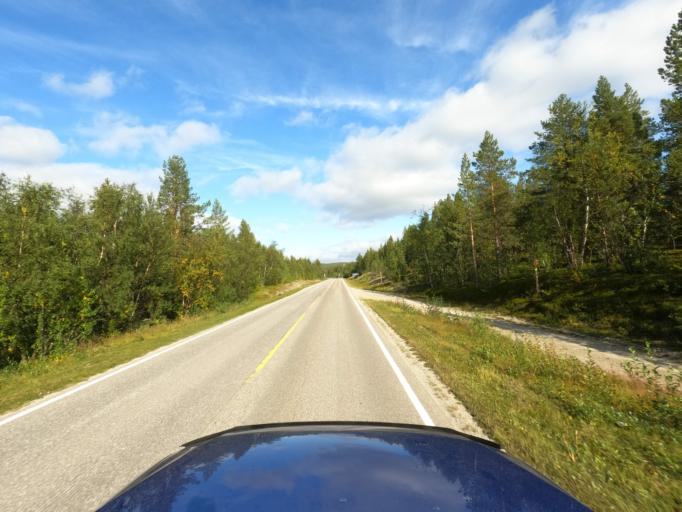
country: NO
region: Finnmark Fylke
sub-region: Porsanger
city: Lakselv
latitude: 69.8985
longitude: 24.9969
